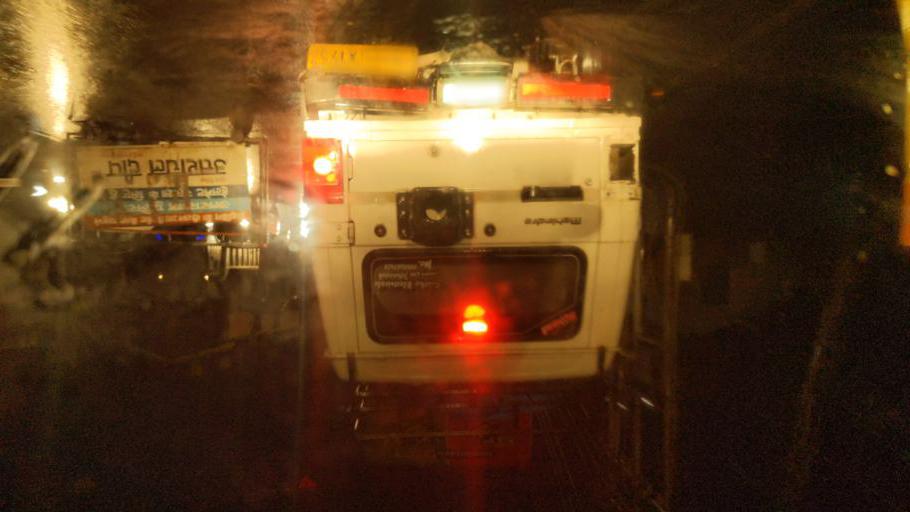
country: IN
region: Uttarakhand
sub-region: Naini Tal
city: Haldwani
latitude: 29.2716
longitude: 79.5442
